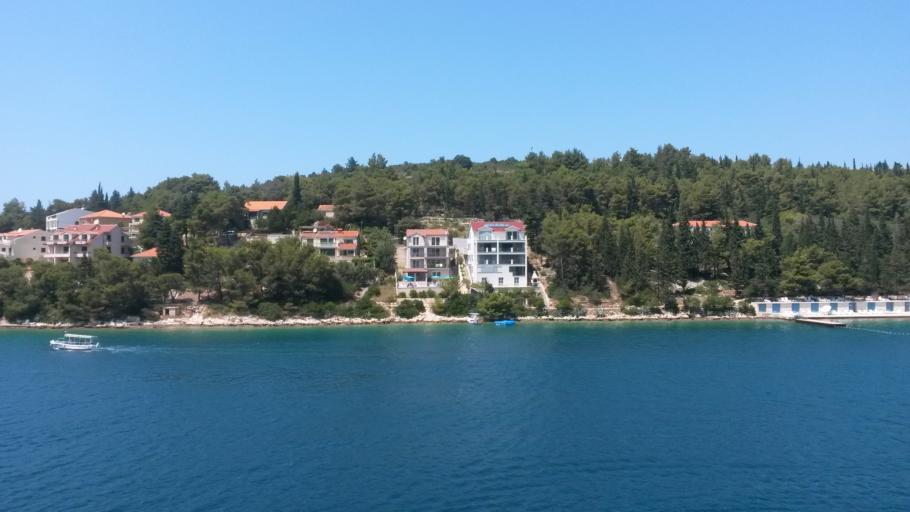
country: HR
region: Dubrovacko-Neretvanska
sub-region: Grad Dubrovnik
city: Vela Luka
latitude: 42.9607
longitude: 16.7095
